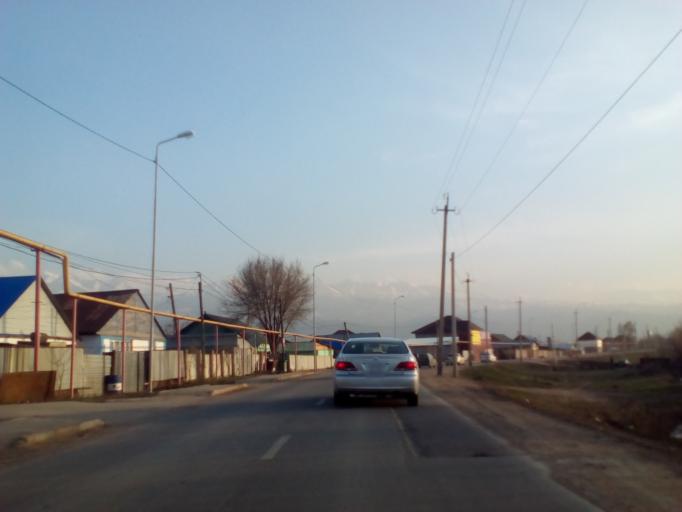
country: KZ
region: Almaty Oblysy
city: Burunday
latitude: 43.2416
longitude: 76.7461
